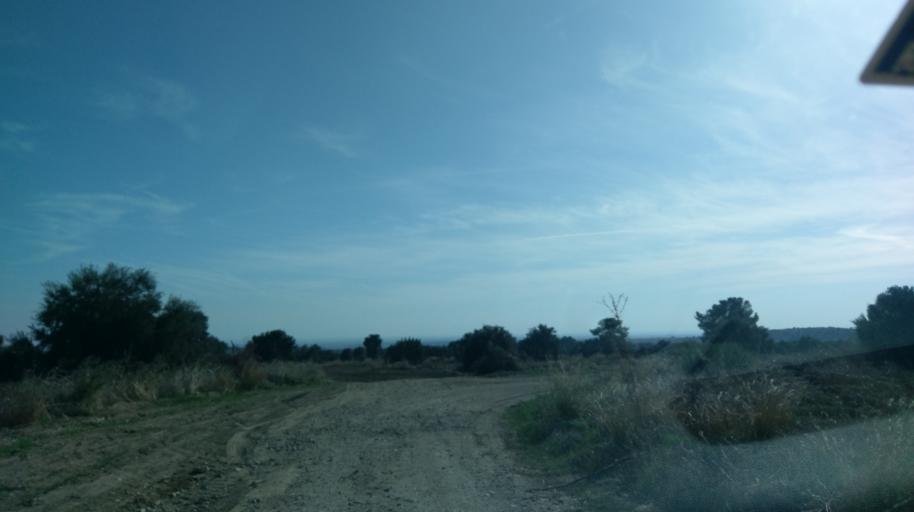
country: CY
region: Ammochostos
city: Trikomo
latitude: 35.3356
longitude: 33.8449
